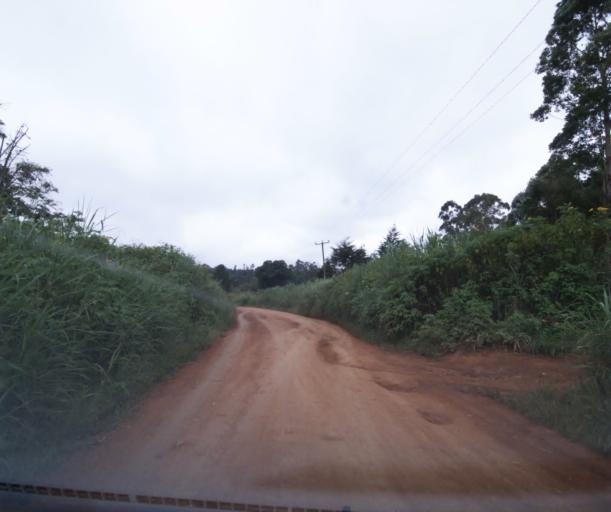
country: CM
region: West
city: Dschang
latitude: 5.5022
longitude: 10.0034
